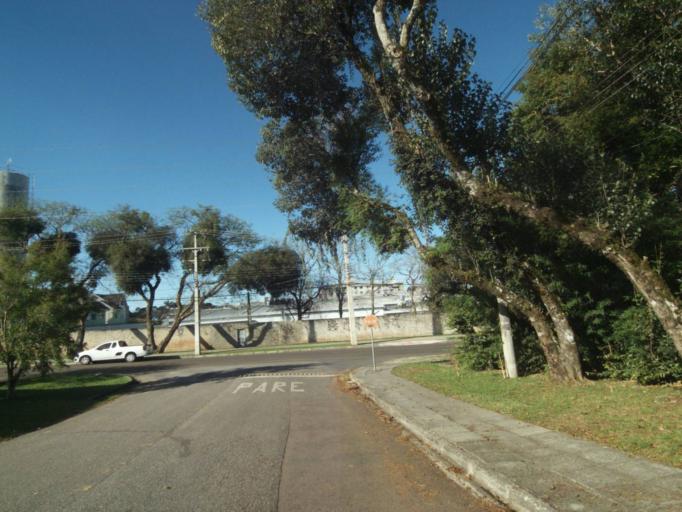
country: BR
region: Parana
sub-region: Curitiba
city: Curitiba
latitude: -25.3890
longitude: -49.2455
